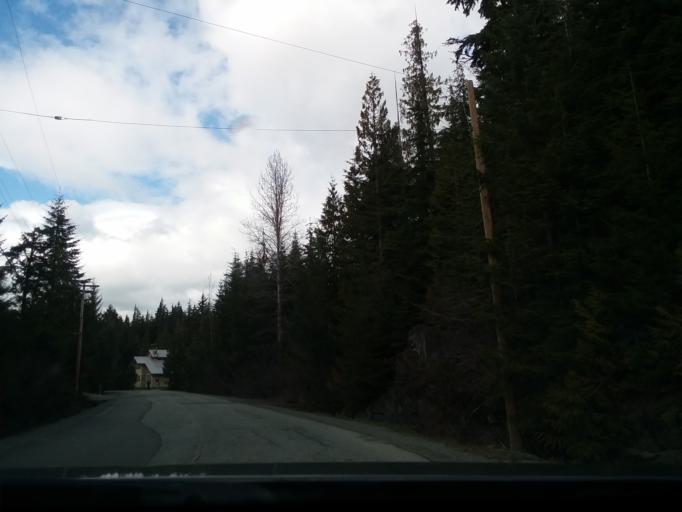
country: CA
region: British Columbia
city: Whistler
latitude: 50.1011
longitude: -122.9859
